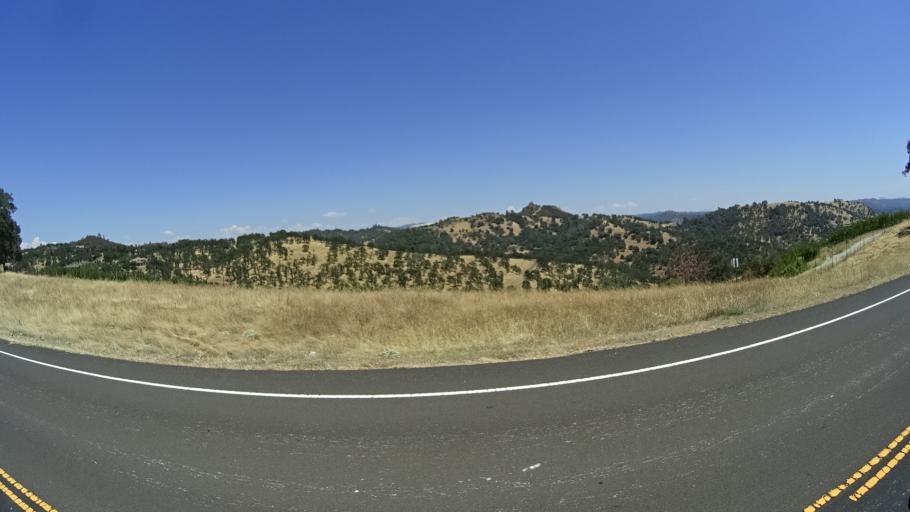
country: US
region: California
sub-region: Calaveras County
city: Angels Camp
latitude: 38.0231
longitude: -120.5271
